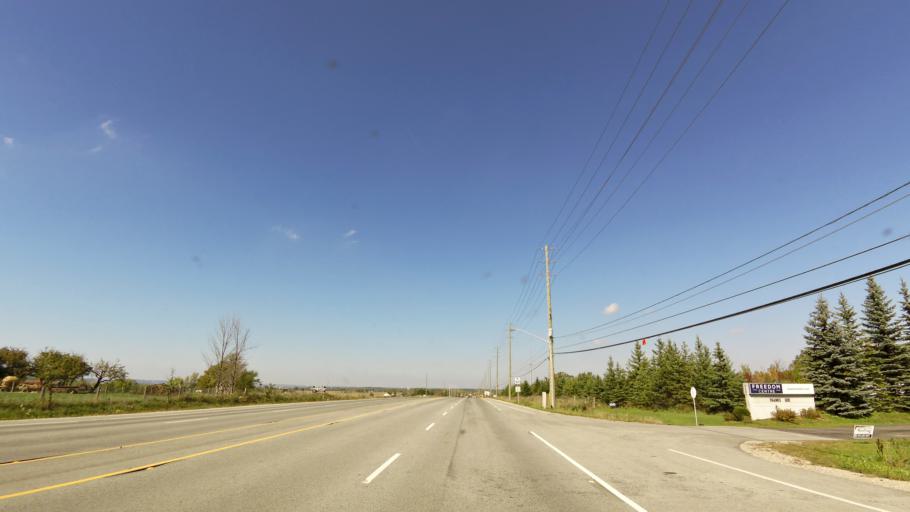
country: CA
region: Ontario
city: Burlington
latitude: 43.4585
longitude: -79.8042
